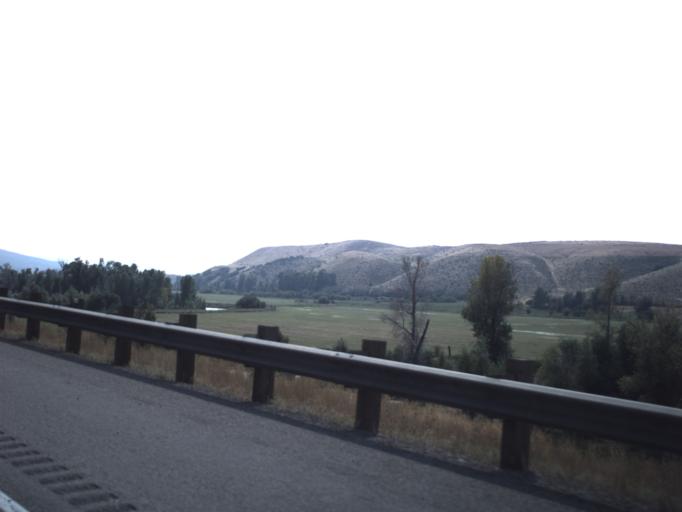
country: US
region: Utah
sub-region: Summit County
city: Coalville
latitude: 40.8486
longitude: -111.3895
